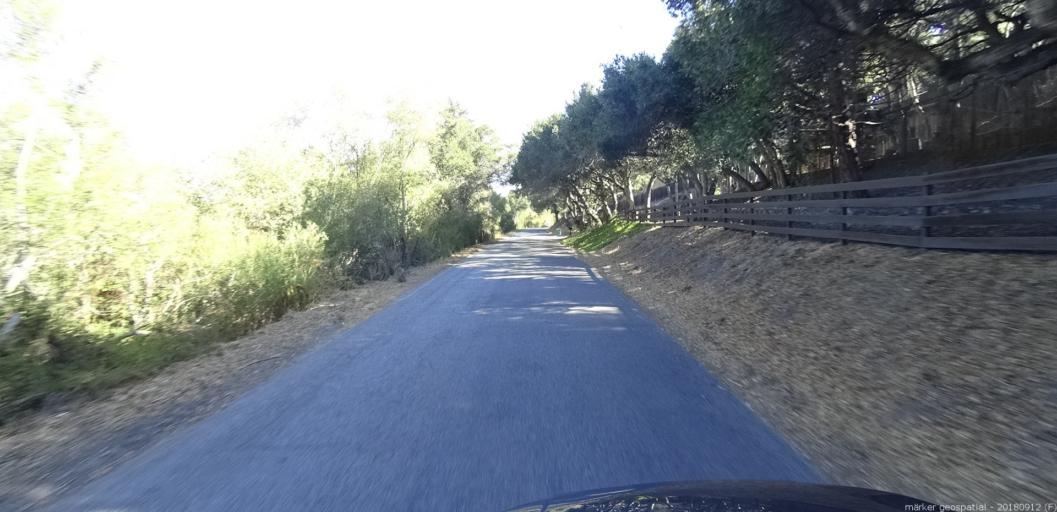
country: US
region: California
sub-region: Monterey County
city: Carmel Valley Village
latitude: 36.5480
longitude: -121.7336
